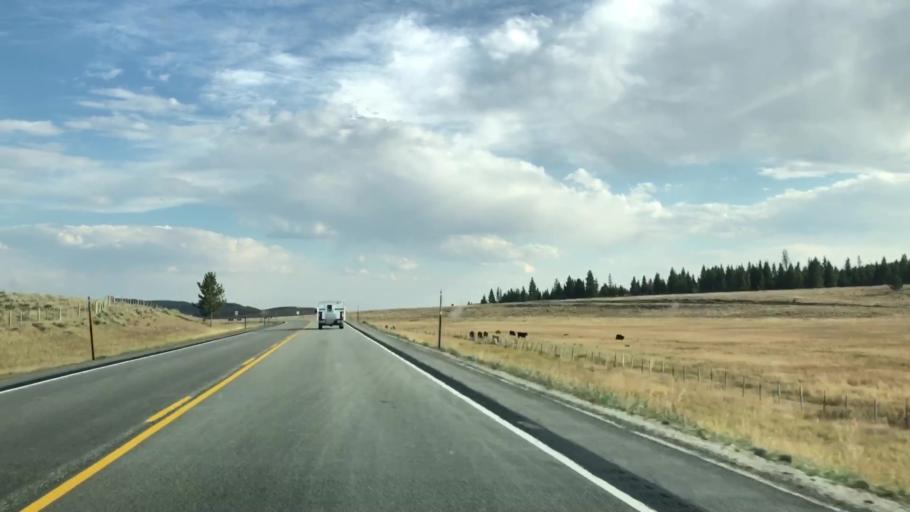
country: US
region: Wyoming
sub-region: Sublette County
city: Pinedale
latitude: 43.1280
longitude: -110.1904
